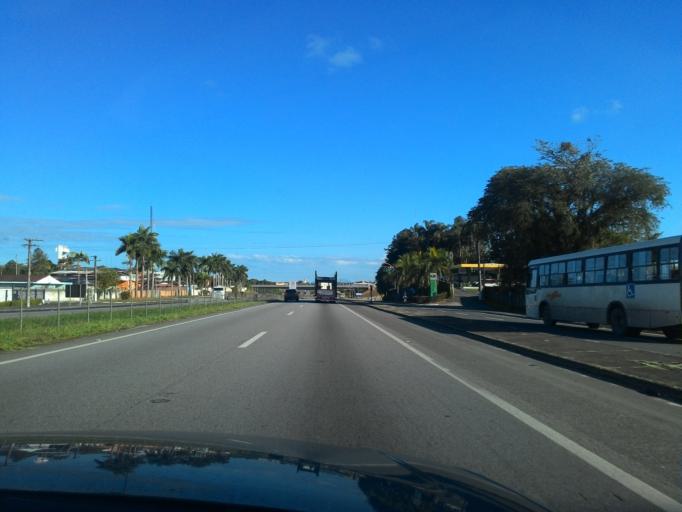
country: BR
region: Sao Paulo
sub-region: Registro
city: Registro
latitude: -24.5041
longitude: -47.8479
